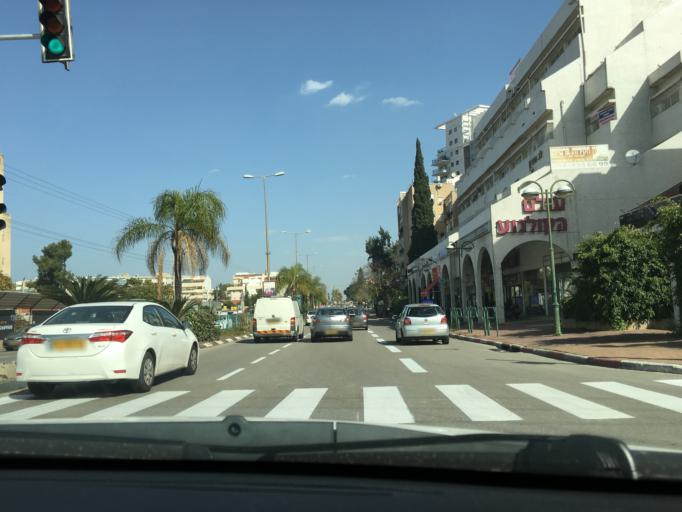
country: IL
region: Central District
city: Kfar Saba
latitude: 32.1769
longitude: 34.8932
